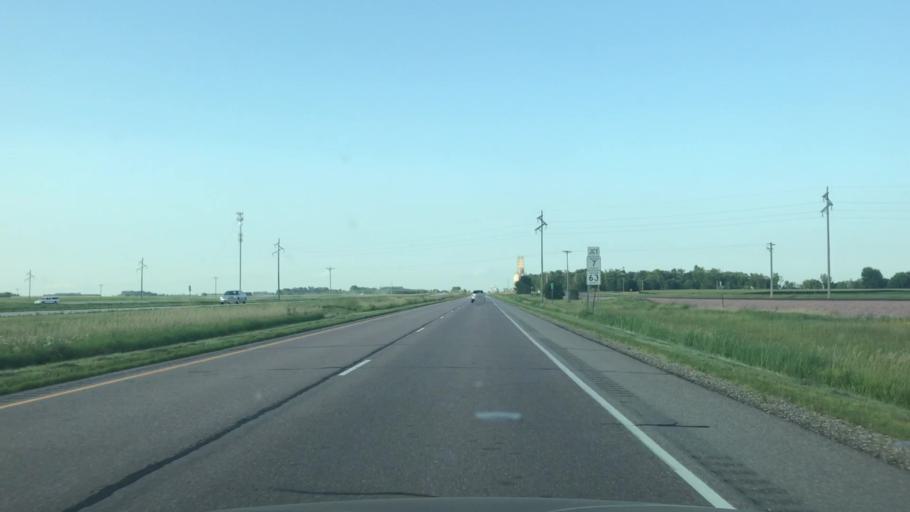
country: US
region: Minnesota
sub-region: Jackson County
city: Lakefield
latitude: 43.7595
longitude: -95.3776
